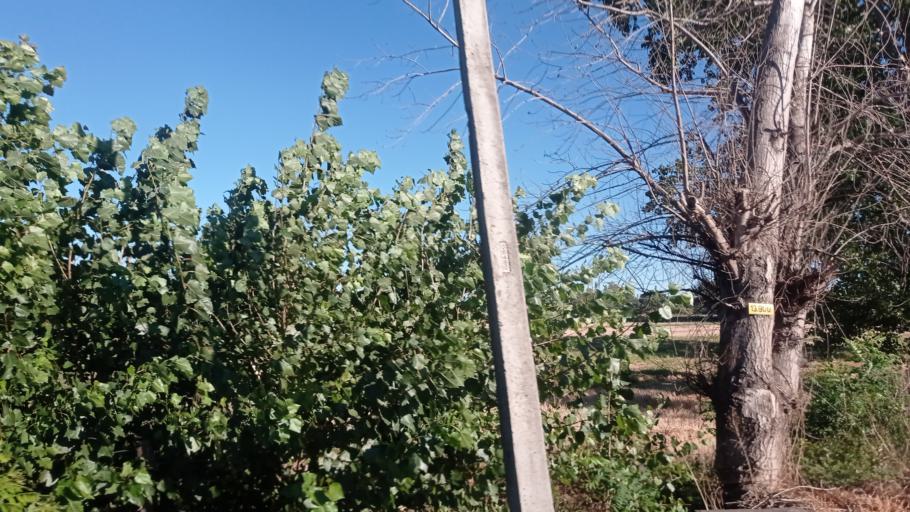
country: CL
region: Biobio
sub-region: Provincia de Biobio
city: Los Angeles
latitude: -37.5128
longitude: -72.5010
